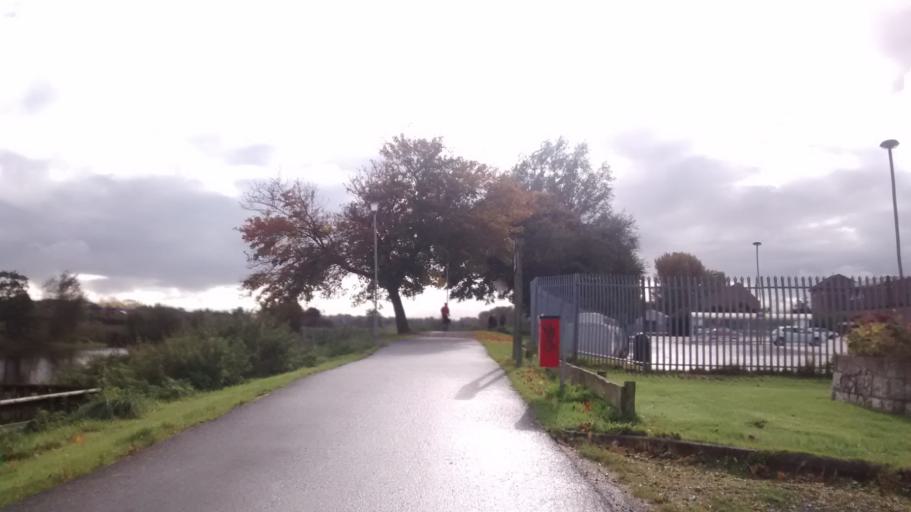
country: GB
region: Northern Ireland
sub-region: Armagh District
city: Portadown
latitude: 54.4233
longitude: -6.4378
